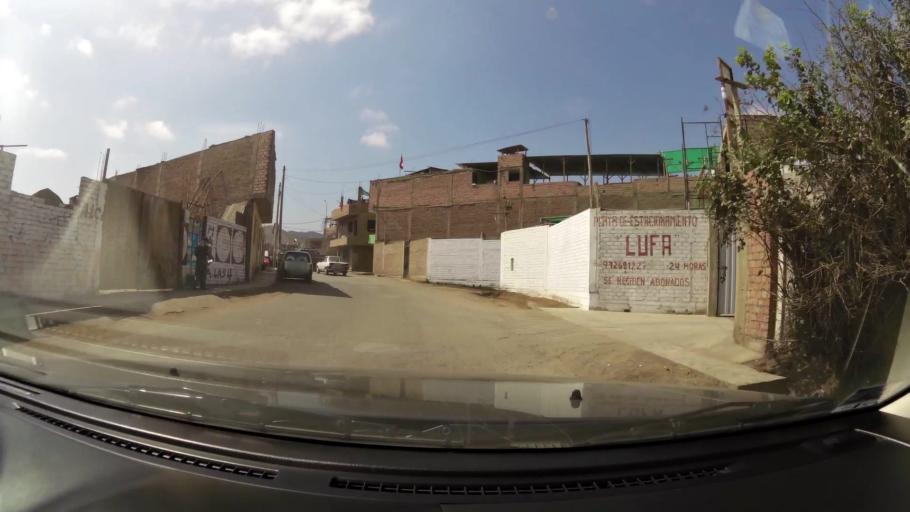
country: PE
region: Lima
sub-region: Provincia de Canete
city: Mala
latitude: -12.6539
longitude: -76.6366
